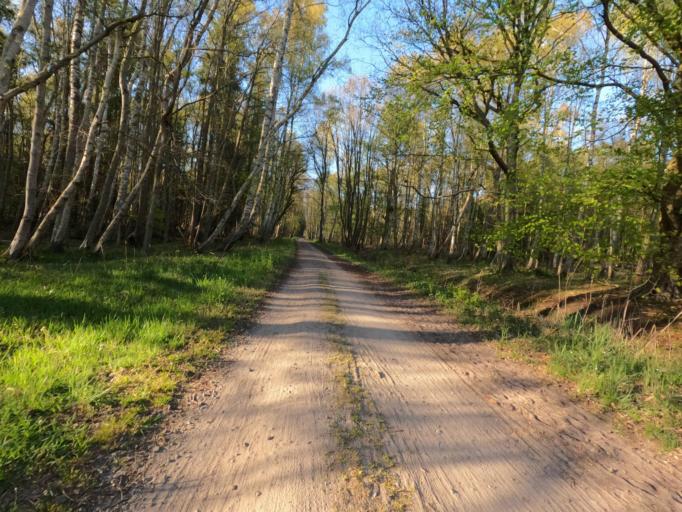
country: DE
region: Mecklenburg-Vorpommern
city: Ostseebad Prerow
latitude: 54.4293
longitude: 12.5382
